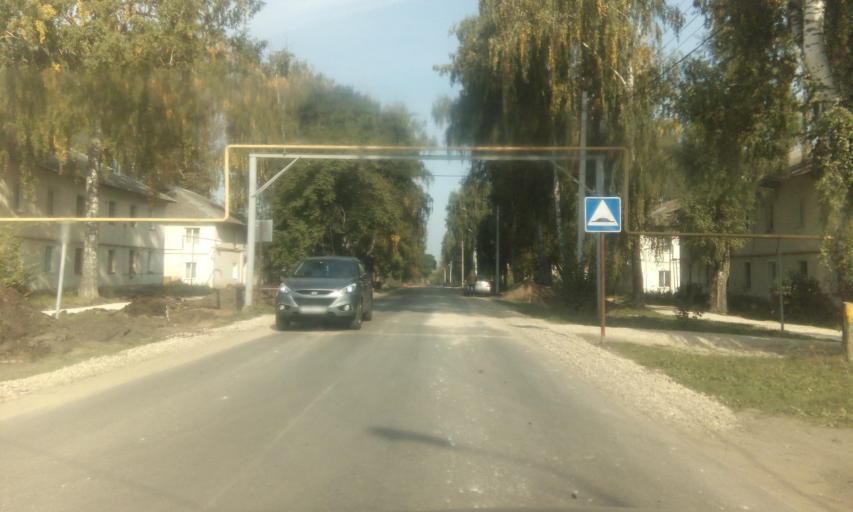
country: RU
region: Tula
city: Partizan
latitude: 53.9503
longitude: 38.0974
